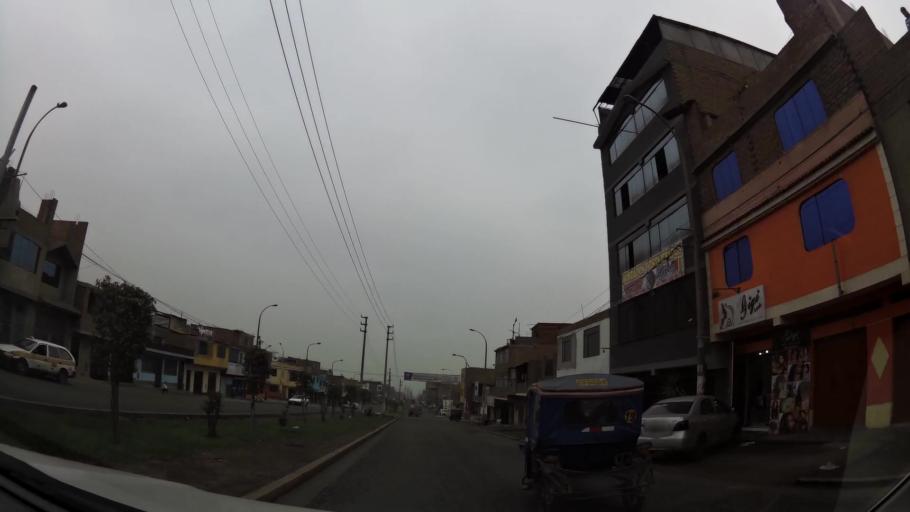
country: PE
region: Lima
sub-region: Lima
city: Independencia
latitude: -11.9433
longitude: -76.9760
